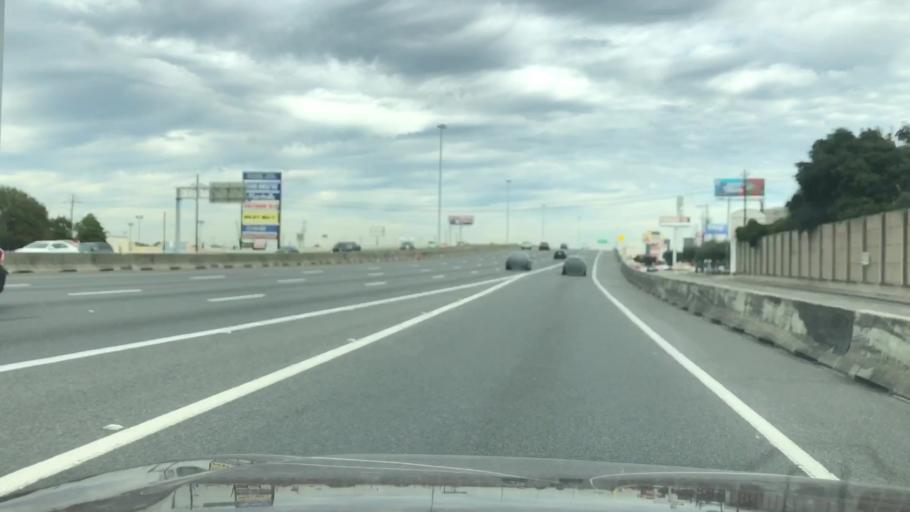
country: US
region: Texas
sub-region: Fort Bend County
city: Meadows Place
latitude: 29.6854
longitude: -95.5323
